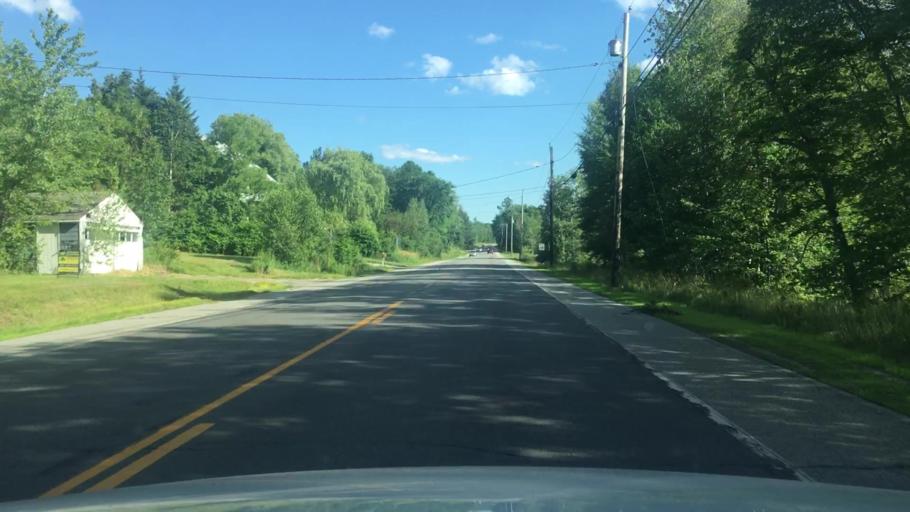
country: US
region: Maine
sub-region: Franklin County
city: Jay
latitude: 44.5456
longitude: -70.2375
